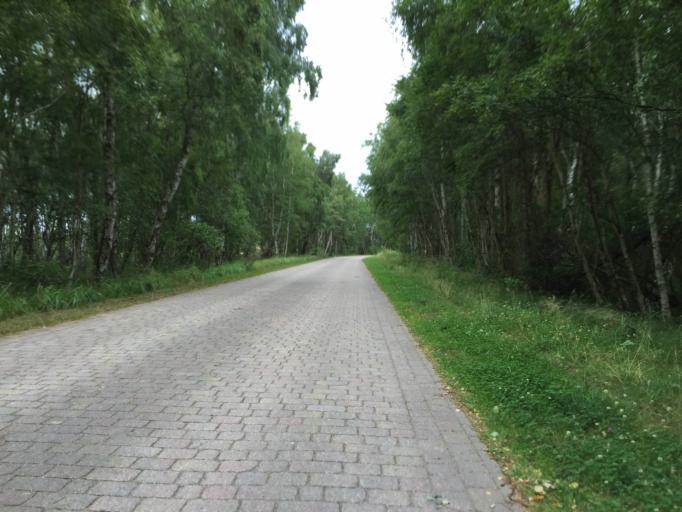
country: DE
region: Mecklenburg-Vorpommern
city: Hiddensee
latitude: 54.5408
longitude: 13.1001
